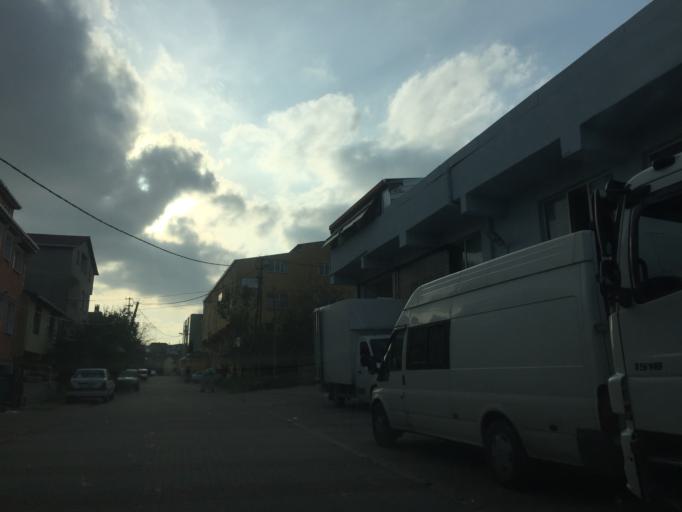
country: TR
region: Istanbul
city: Sultanbeyli
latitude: 40.9483
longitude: 29.2966
